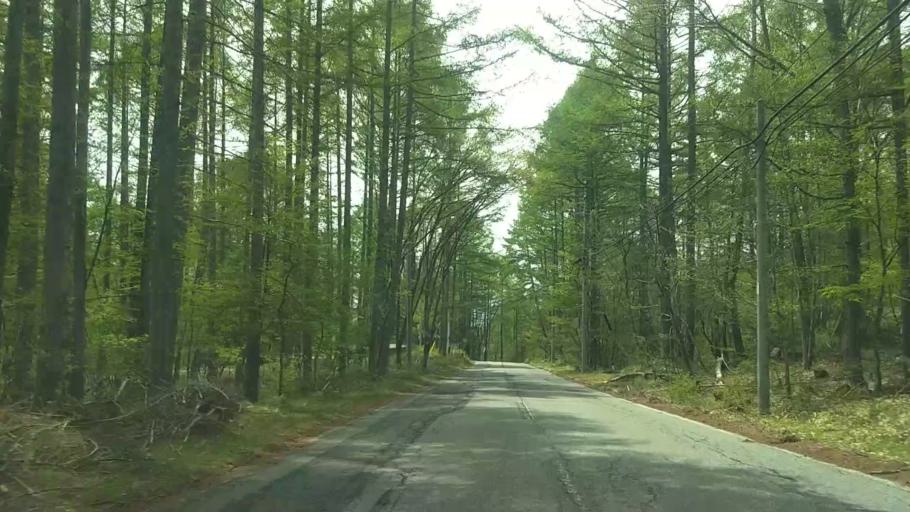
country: JP
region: Nagano
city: Chino
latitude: 36.0437
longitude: 138.2966
